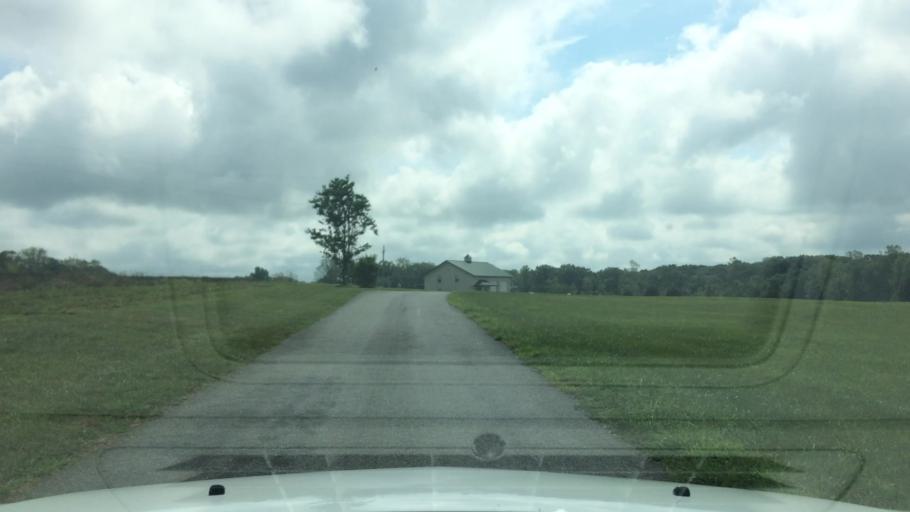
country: US
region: North Carolina
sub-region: Yadkin County
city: Jonesville
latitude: 36.0973
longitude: -80.8527
